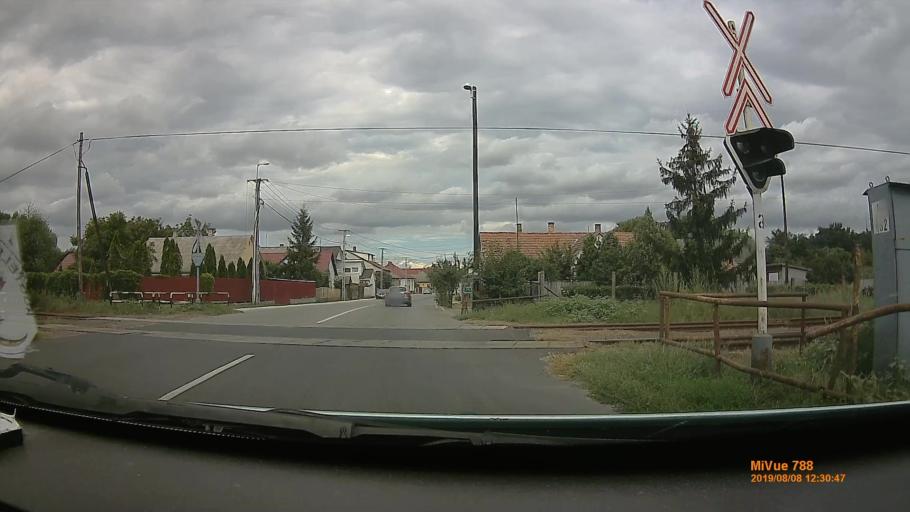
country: HU
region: Szabolcs-Szatmar-Bereg
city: Nyirbator
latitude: 47.8415
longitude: 22.1218
